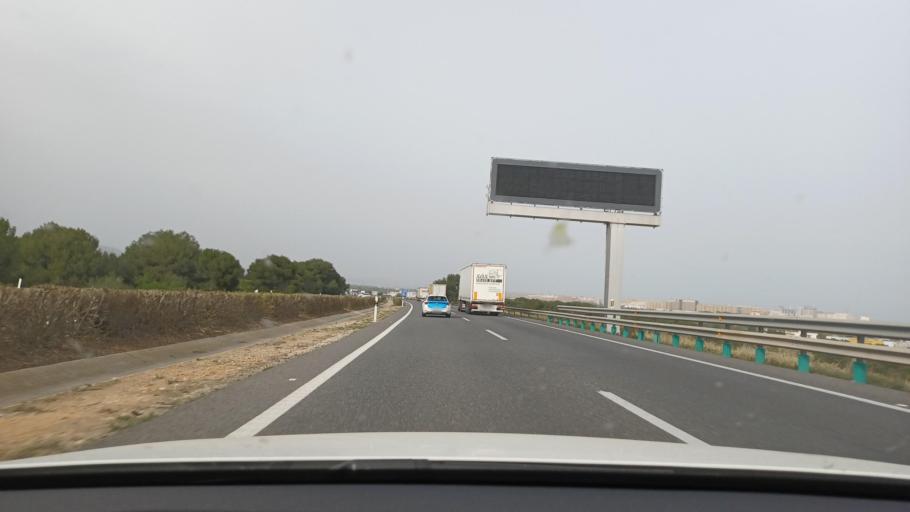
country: ES
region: Valencia
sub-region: Provincia de Castello
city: Orpesa/Oropesa del Mar
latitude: 40.0960
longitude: 0.1266
